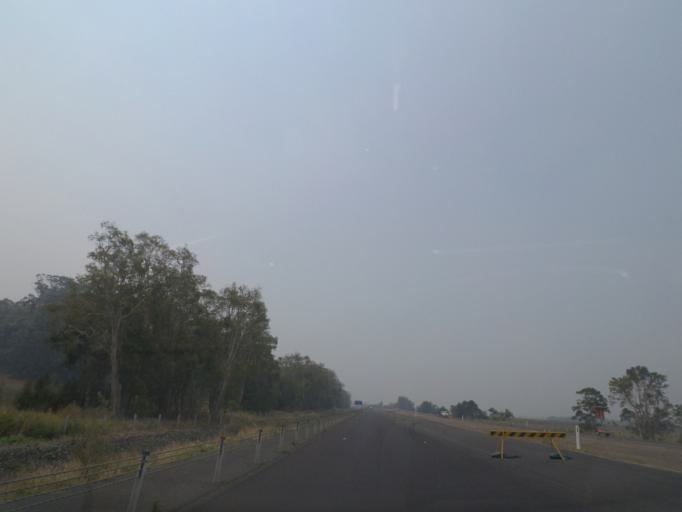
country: AU
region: New South Wales
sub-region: Ballina
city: Ballina
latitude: -28.8813
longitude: 153.4855
